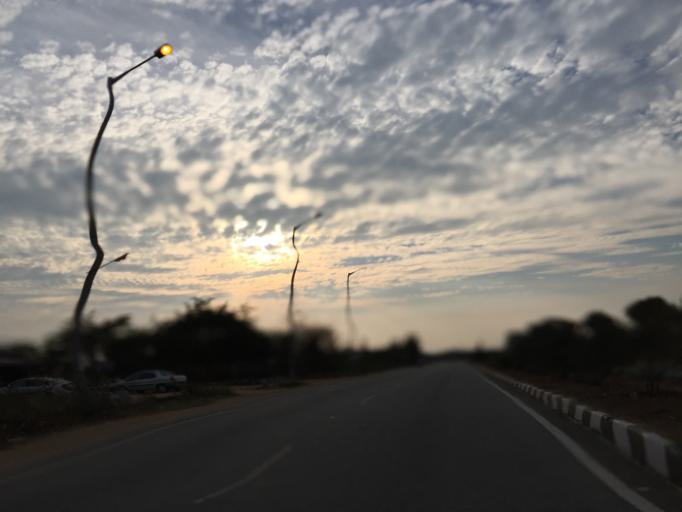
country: IN
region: Karnataka
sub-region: Kolar
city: Kolar
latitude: 13.1469
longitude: 78.2529
